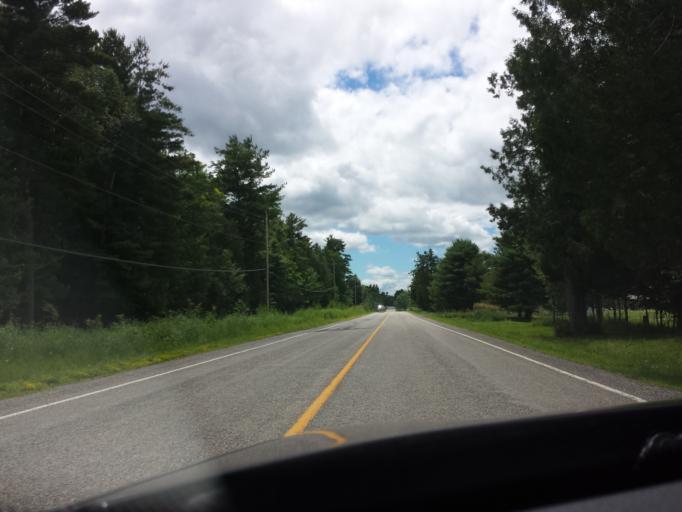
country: CA
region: Ontario
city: Perth
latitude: 44.8286
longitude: -76.2168
